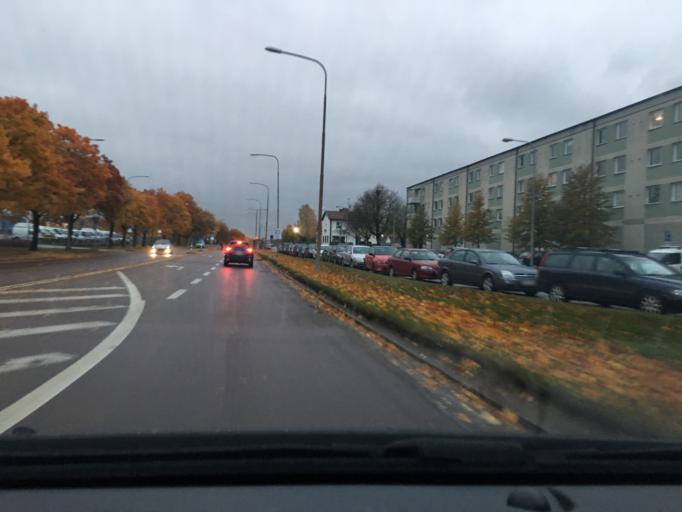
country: SE
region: Stockholm
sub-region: Stockholms Kommun
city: Kista
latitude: 59.3779
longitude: 17.9067
